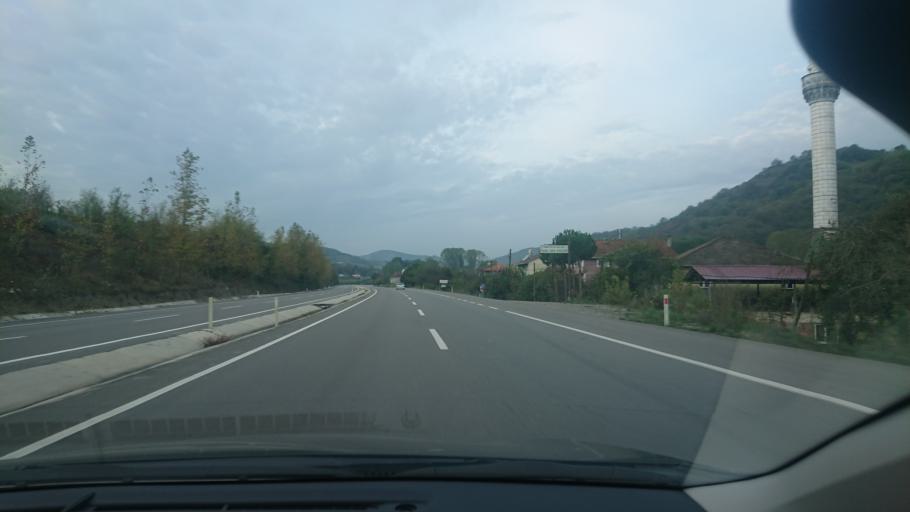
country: TR
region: Zonguldak
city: Gokcebey
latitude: 41.3324
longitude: 32.0687
